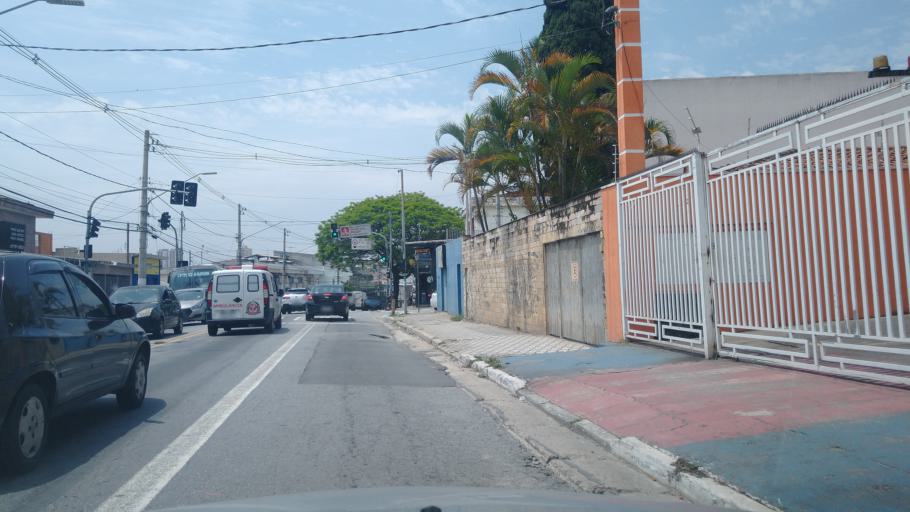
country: BR
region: Sao Paulo
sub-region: Sao Paulo
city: Sao Paulo
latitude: -23.4724
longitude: -46.6731
